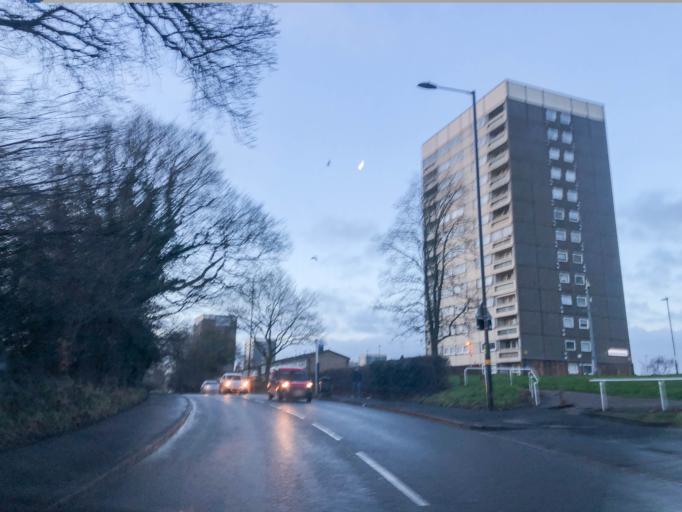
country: GB
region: England
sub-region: Solihull
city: Tidbury Green
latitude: 52.4102
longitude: -1.8868
